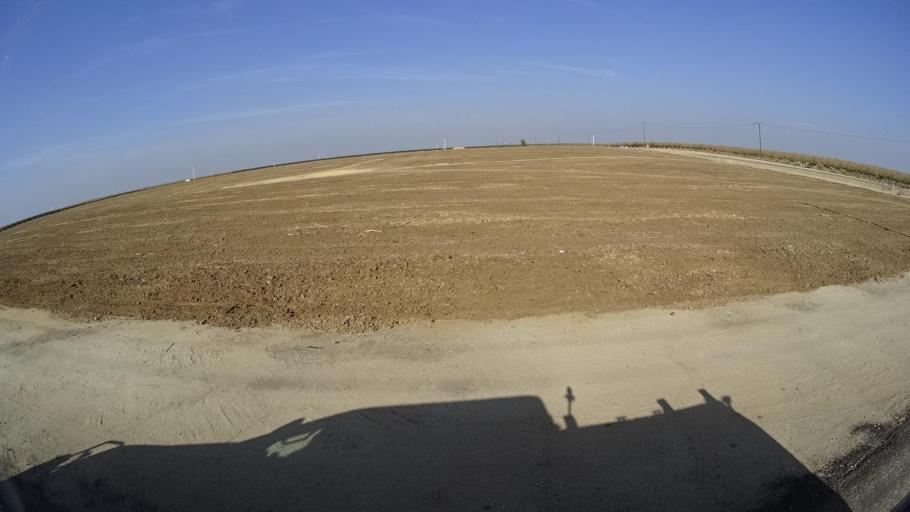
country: US
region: California
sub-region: Kern County
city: McFarland
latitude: 35.6308
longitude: -119.1696
